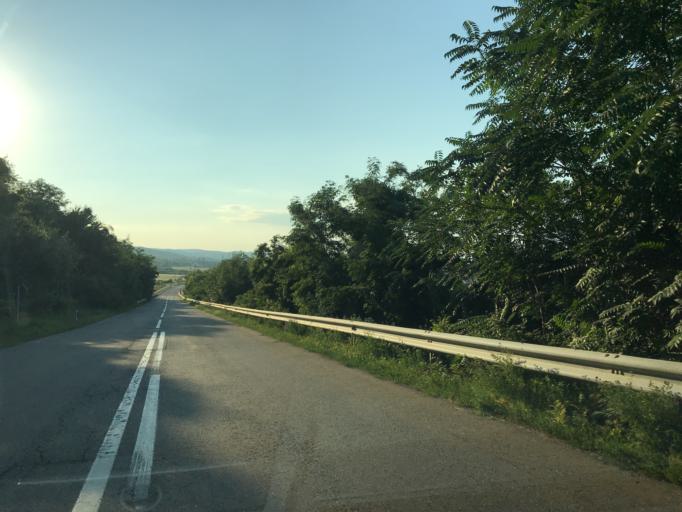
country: RO
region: Mehedinti
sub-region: Comuna Gogosu
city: Ostrovu Mare
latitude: 44.4267
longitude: 22.4736
